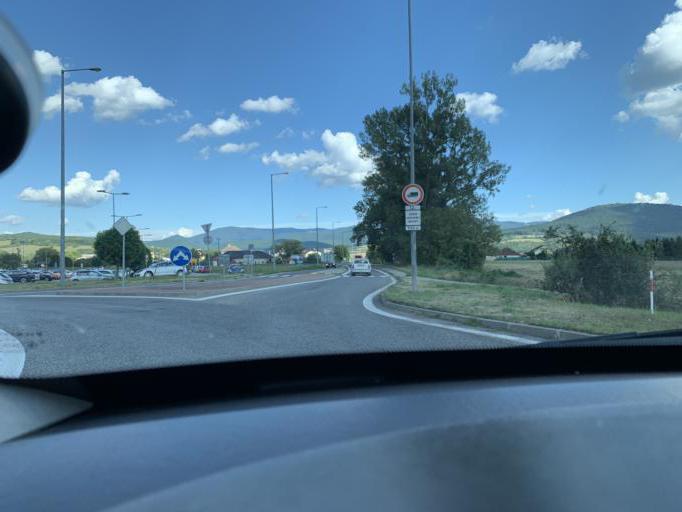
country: SK
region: Trenciansky
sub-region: Okres Nove Mesto nad Vahom
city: Nove Mesto nad Vahom
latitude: 48.7611
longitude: 17.8780
